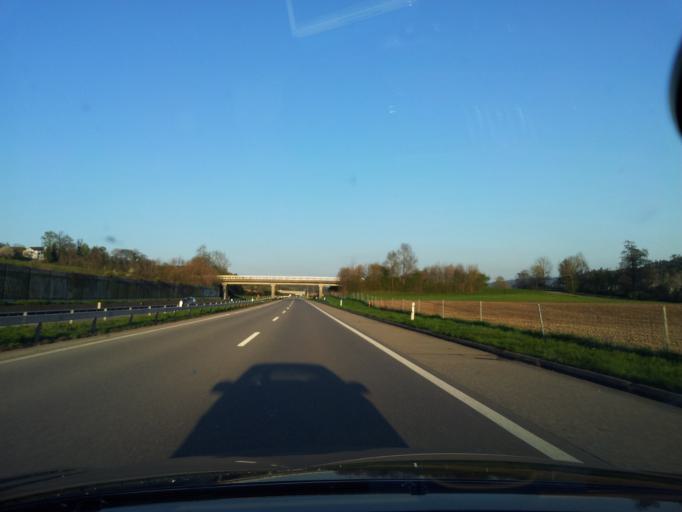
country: CH
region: Bern
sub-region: Seeland District
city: Schupfen
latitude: 47.0427
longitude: 7.4014
